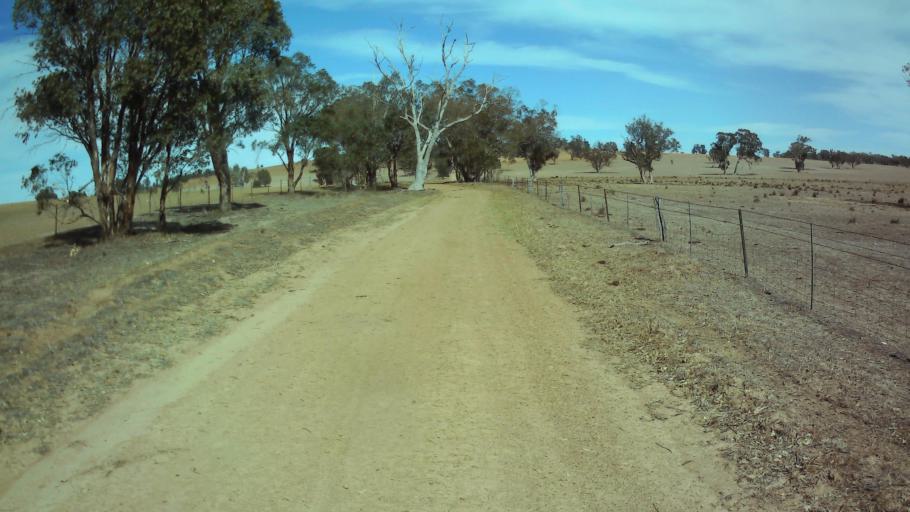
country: AU
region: New South Wales
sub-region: Weddin
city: Grenfell
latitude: -33.6808
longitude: 148.2729
